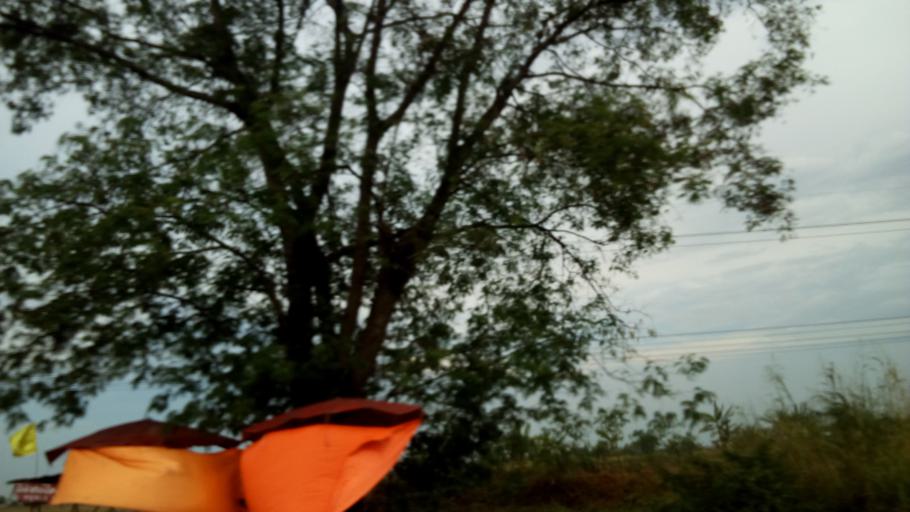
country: TH
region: Phra Nakhon Si Ayutthaya
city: Phra Nakhon Si Ayutthaya
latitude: 14.2966
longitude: 100.5247
